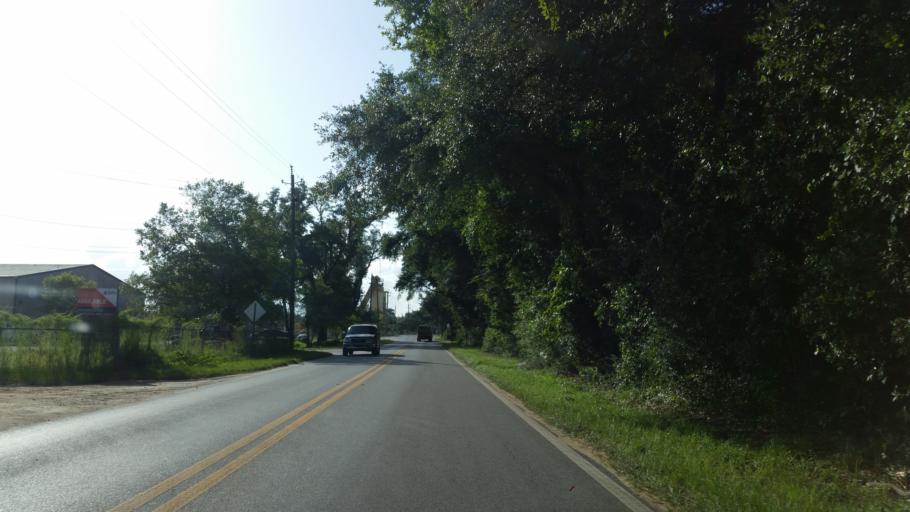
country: US
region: Florida
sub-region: Santa Rosa County
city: Bagdad
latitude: 30.5847
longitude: -87.0614
